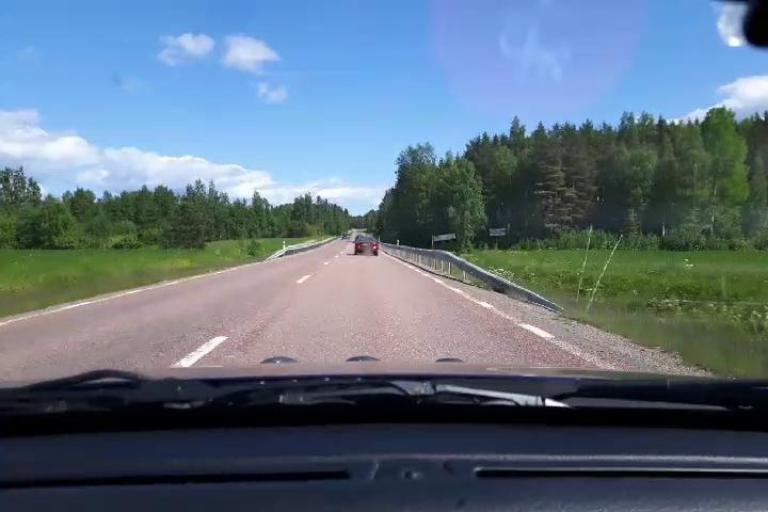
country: SE
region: Gaevleborg
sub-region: Hudiksvalls Kommun
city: Delsbo
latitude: 61.7974
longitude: 16.5065
